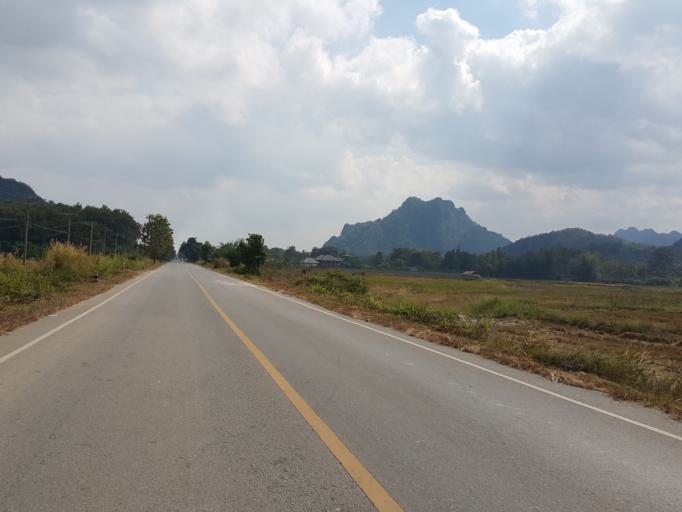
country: TH
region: Sukhothai
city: Thung Saliam
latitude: 17.3339
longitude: 99.4945
